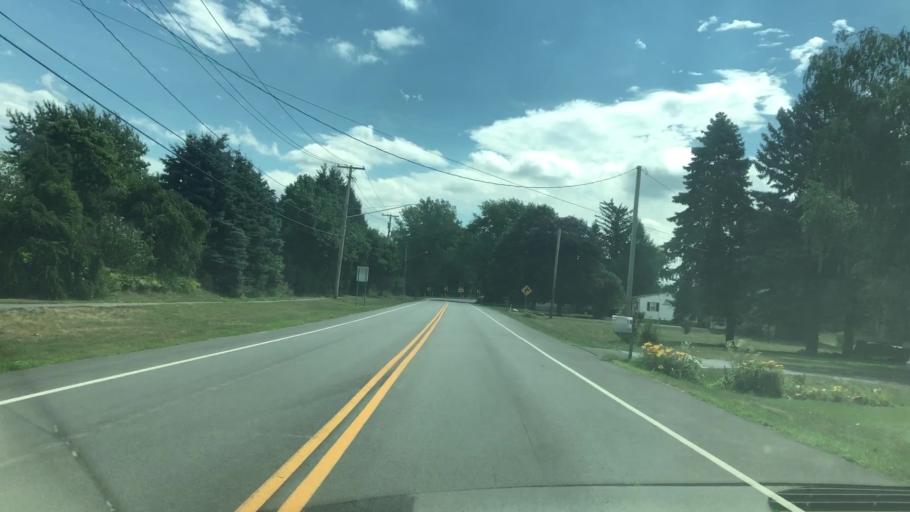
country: US
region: New York
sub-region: Monroe County
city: Fairport
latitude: 43.0795
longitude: -77.3943
